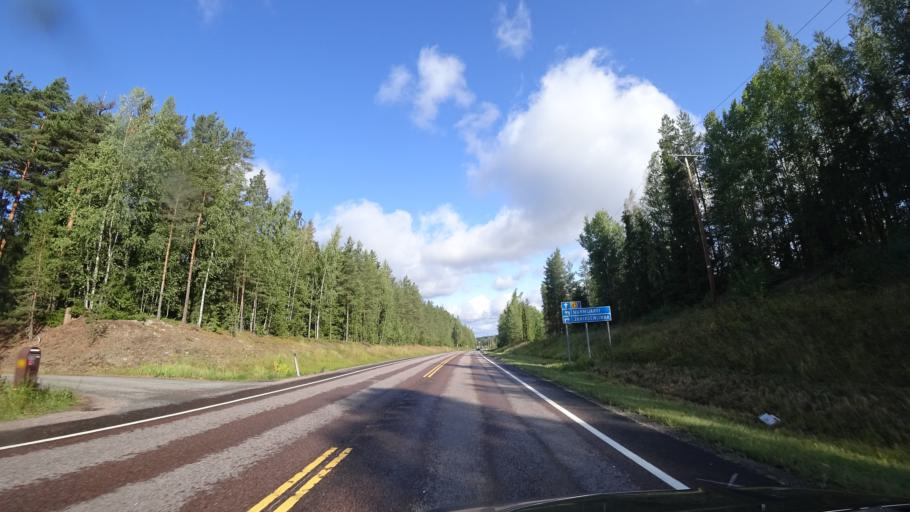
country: FI
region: Uusimaa
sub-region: Helsinki
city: Nurmijaervi
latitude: 60.5074
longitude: 24.9295
